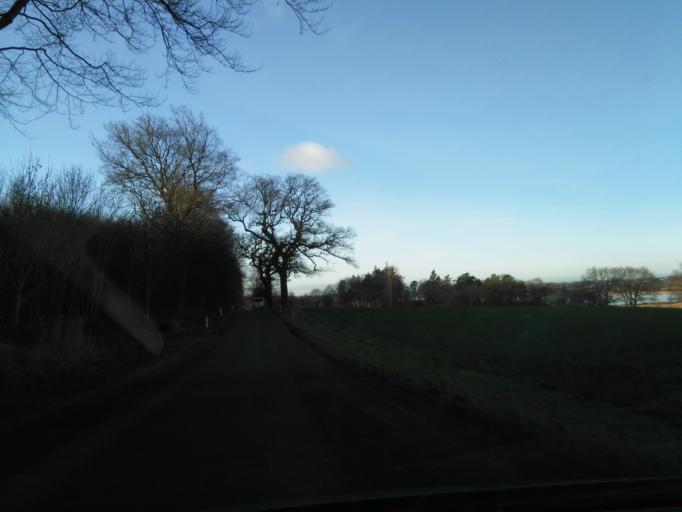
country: DK
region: Central Jutland
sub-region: Arhus Kommune
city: Stavtrup
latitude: 56.1411
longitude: 10.0977
